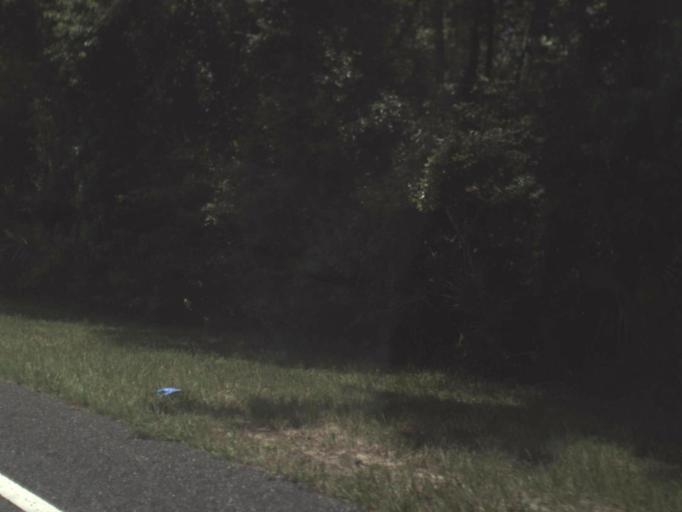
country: US
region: Florida
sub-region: Taylor County
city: Steinhatchee
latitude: 29.6872
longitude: -83.2685
